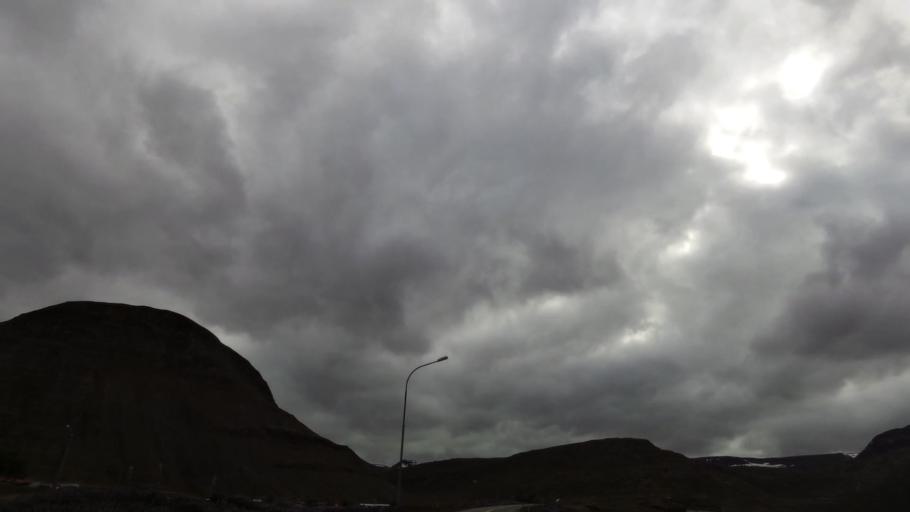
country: IS
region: Westfjords
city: Isafjoerdur
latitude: 66.0591
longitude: -23.1721
